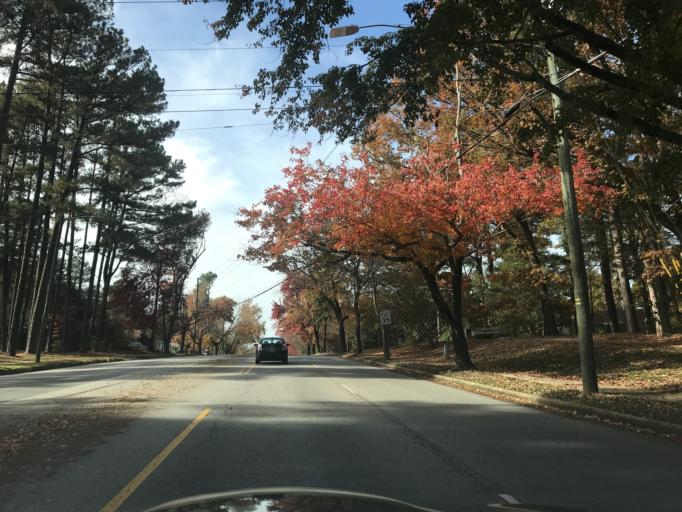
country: US
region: North Carolina
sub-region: Wake County
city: West Raleigh
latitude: 35.8517
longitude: -78.6257
